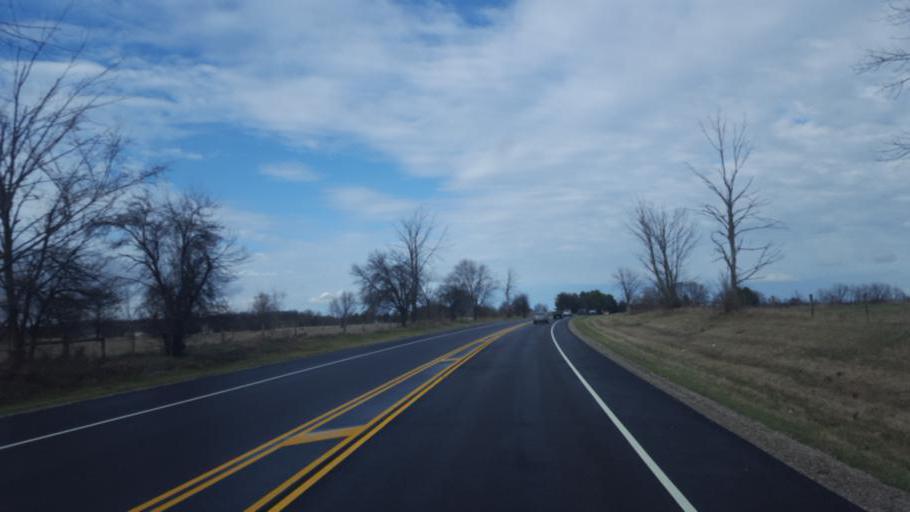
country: US
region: Ohio
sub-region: Delaware County
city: Sunbury
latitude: 40.2103
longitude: -82.9036
